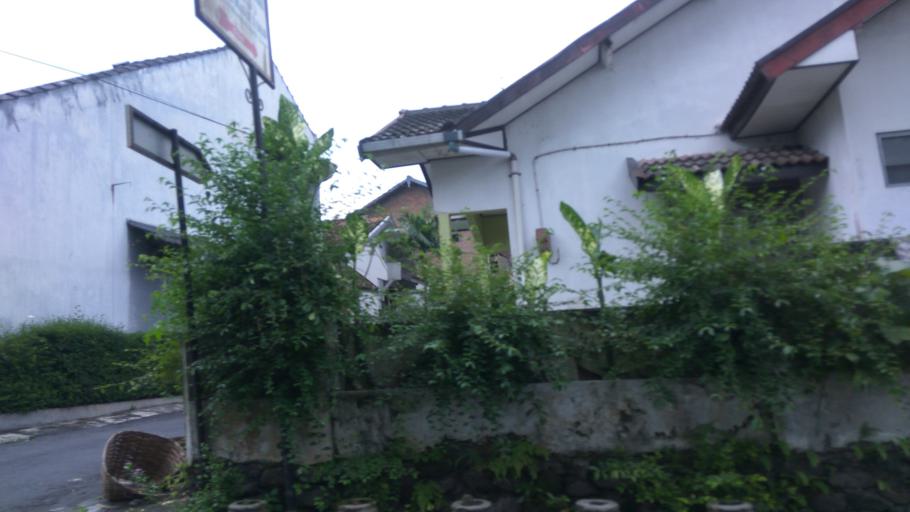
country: ID
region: Daerah Istimewa Yogyakarta
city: Depok
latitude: -7.7388
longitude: 110.4088
